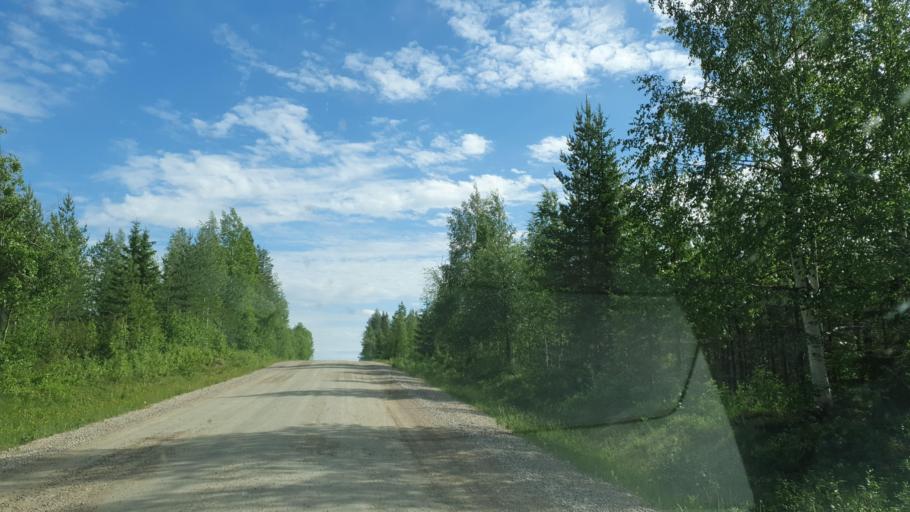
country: FI
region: Kainuu
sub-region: Kehys-Kainuu
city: Kuhmo
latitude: 64.4727
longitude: 29.5346
